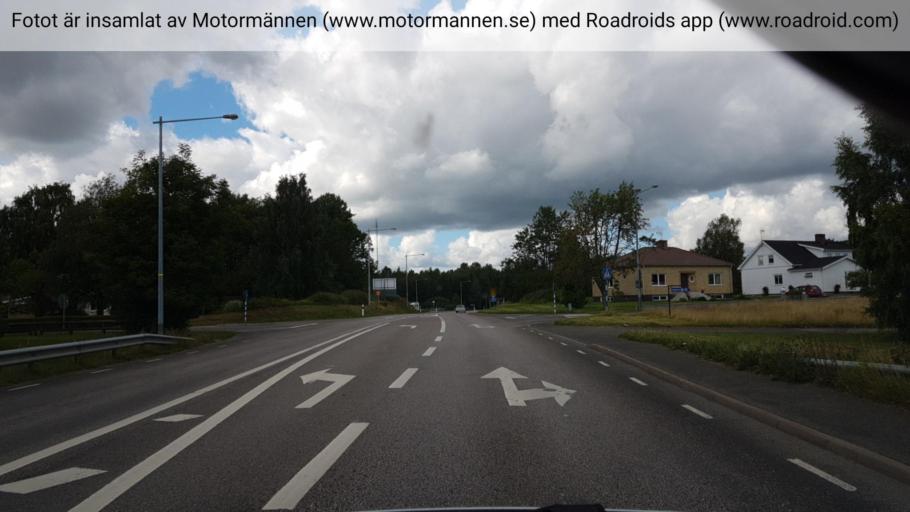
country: SE
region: Vaestra Goetaland
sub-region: Falkopings Kommun
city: Falkoeping
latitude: 58.0271
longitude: 13.5511
